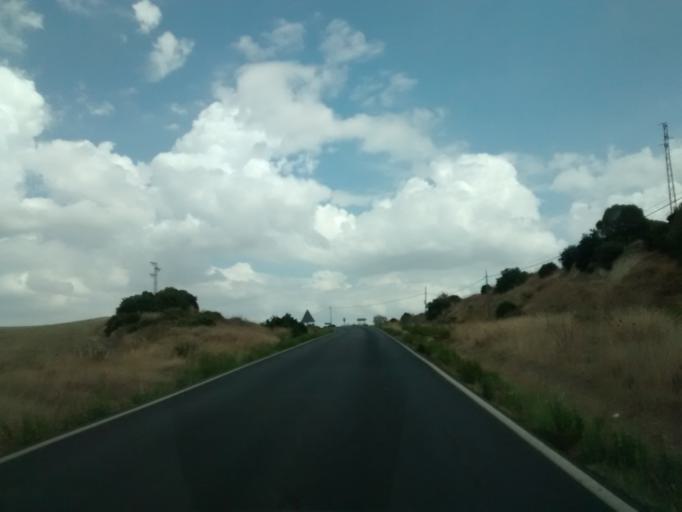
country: ES
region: Andalusia
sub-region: Provincia de Cadiz
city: Arcos de la Frontera
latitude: 36.7292
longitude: -5.8272
